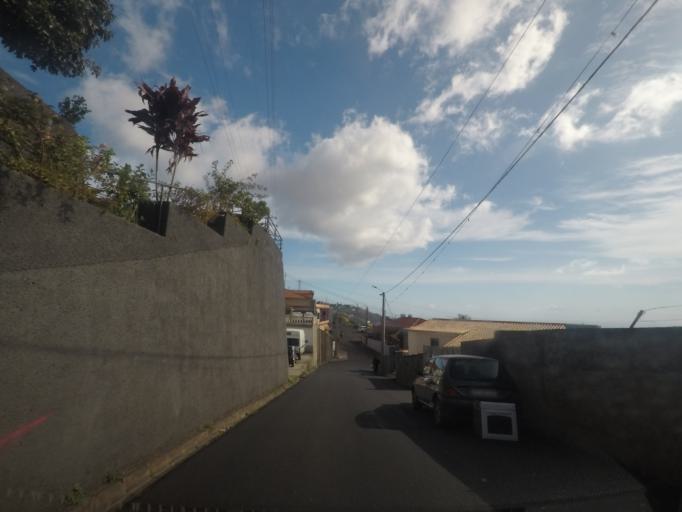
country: PT
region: Madeira
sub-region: Funchal
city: Nossa Senhora do Monte
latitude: 32.6754
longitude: -16.8934
